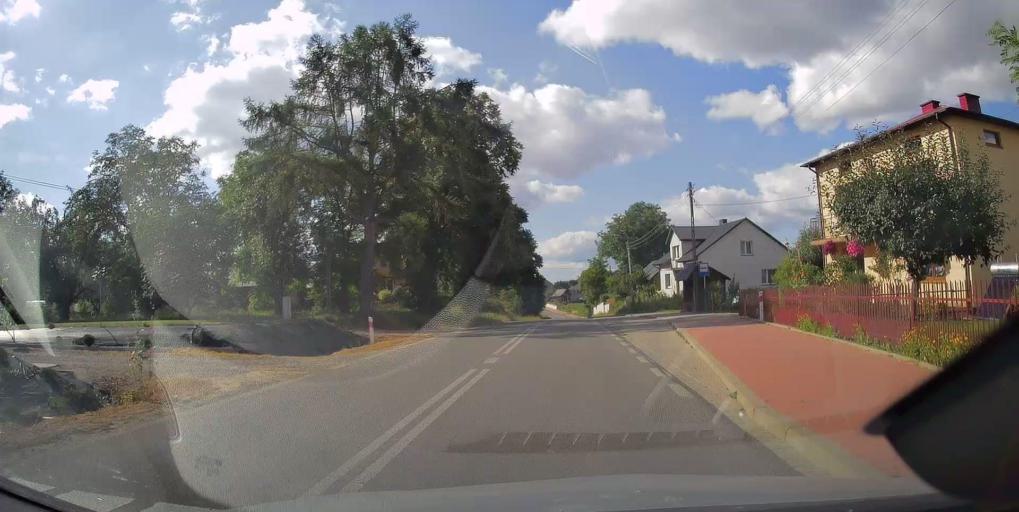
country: PL
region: Swietokrzyskie
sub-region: Powiat kielecki
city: Nowa Slupia
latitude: 50.8753
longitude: 21.0700
